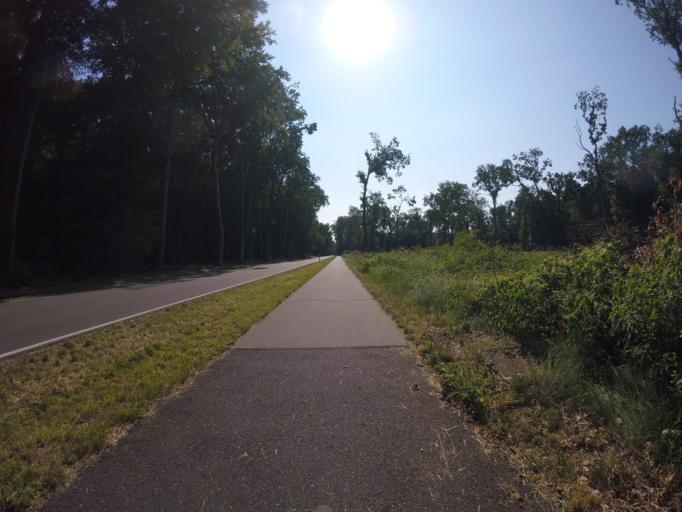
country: DE
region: Brandenburg
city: Mullrose
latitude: 52.2597
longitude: 14.3819
